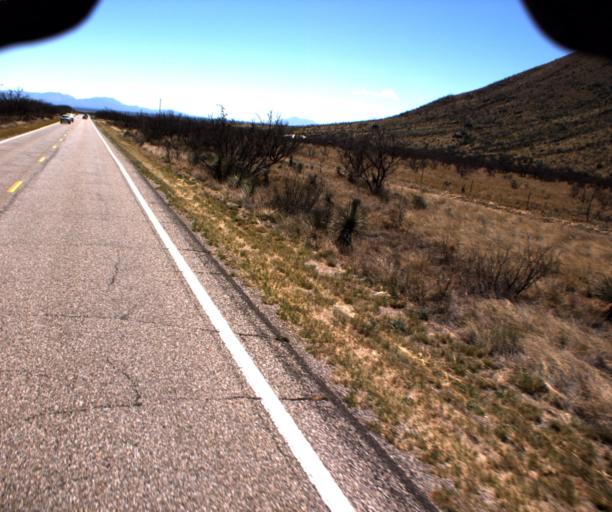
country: US
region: Arizona
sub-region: Cochise County
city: Huachuca City
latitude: 31.7012
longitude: -110.4308
